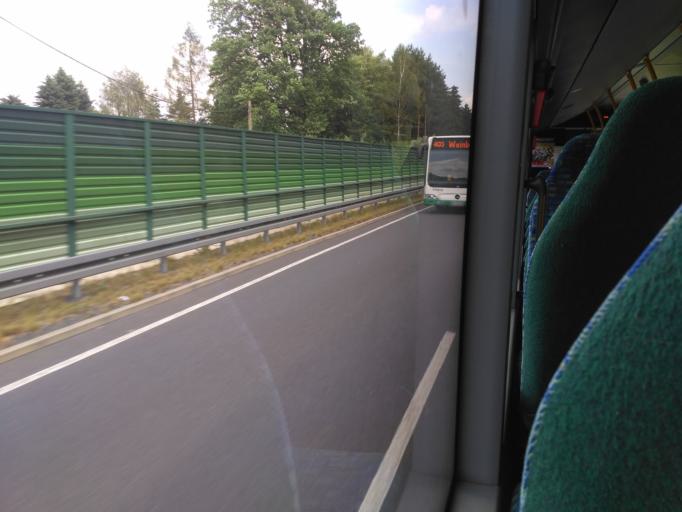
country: DE
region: Saxony
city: Coswig
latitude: 51.1594
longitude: 13.6273
